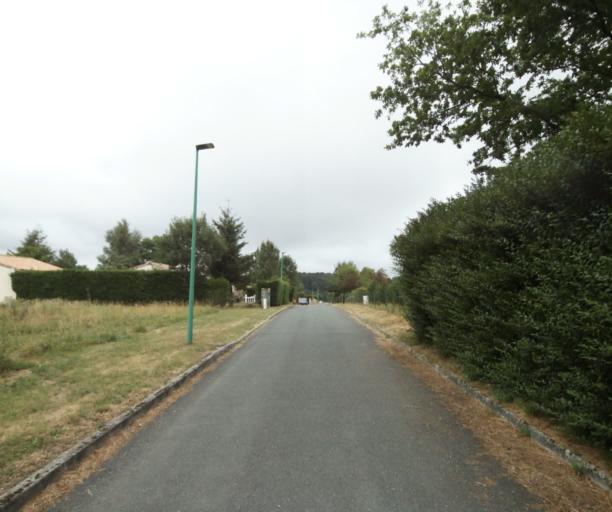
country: FR
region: Midi-Pyrenees
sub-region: Departement du Tarn
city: Soreze
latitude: 43.4061
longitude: 2.0785
